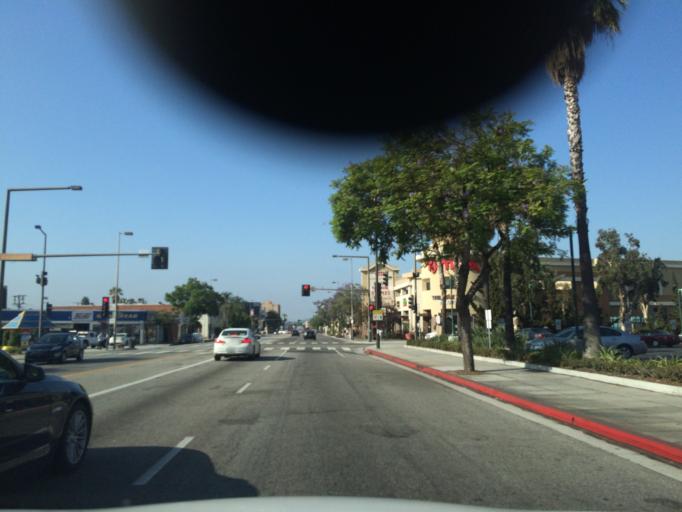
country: US
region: California
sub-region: Los Angeles County
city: Glendale
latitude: 34.1505
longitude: -118.2456
